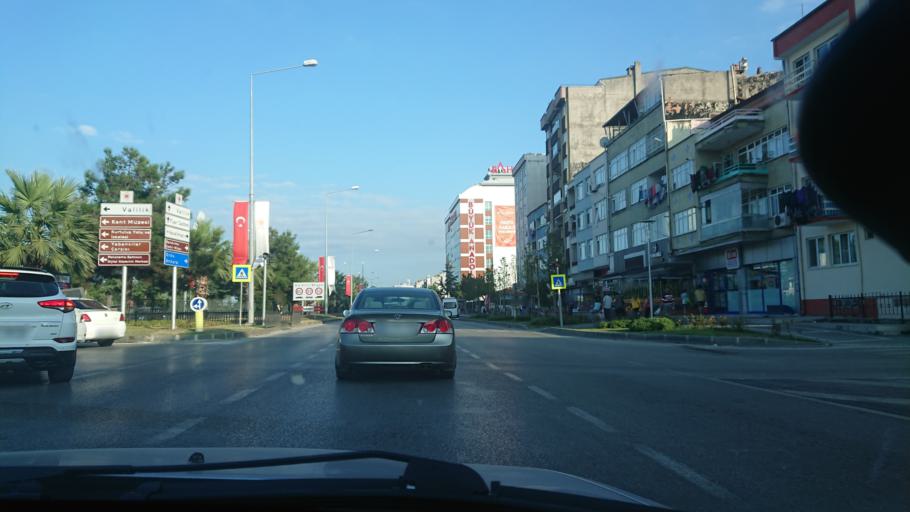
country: TR
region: Samsun
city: Samsun
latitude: 41.2855
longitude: 36.3416
